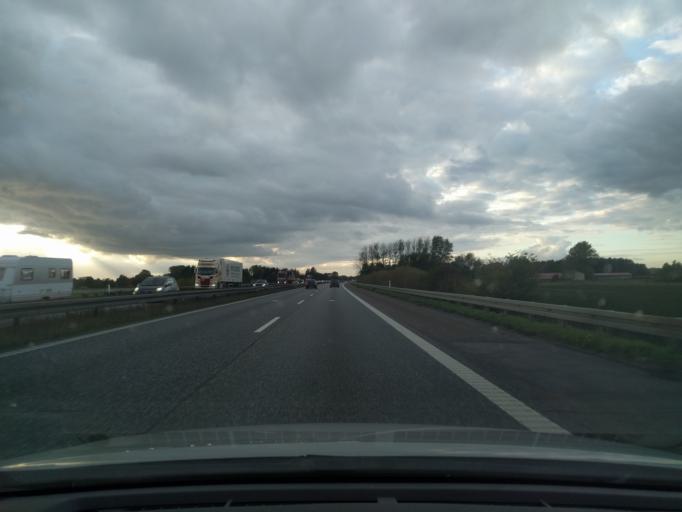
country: DK
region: Zealand
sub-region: Soro Kommune
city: Frederiksberg
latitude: 55.4481
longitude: 11.6477
